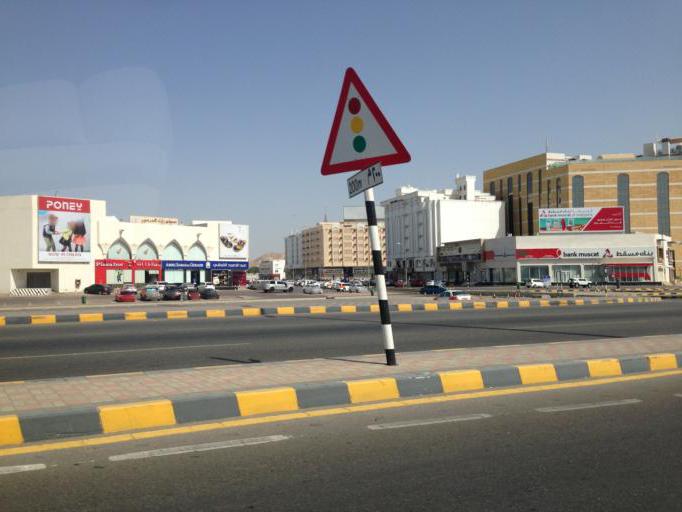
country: OM
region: Muhafazat Masqat
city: Muscat
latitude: 23.6138
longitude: 58.4935
